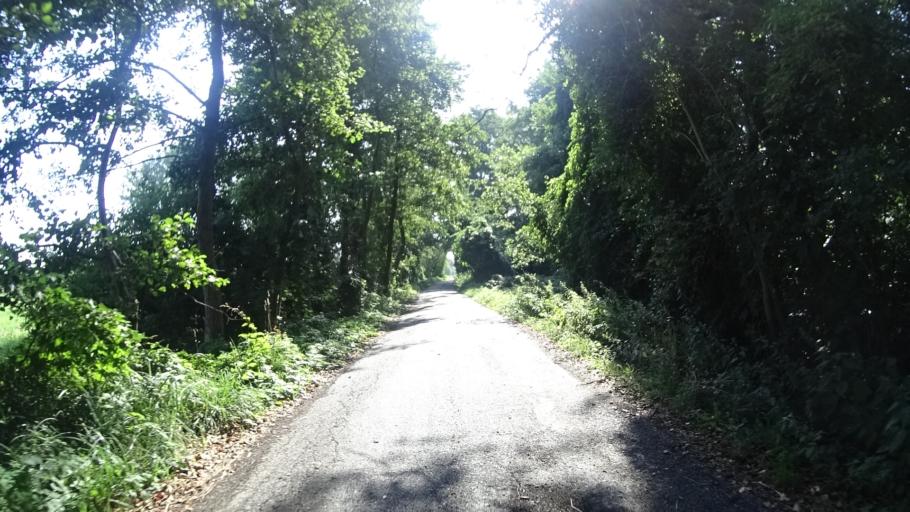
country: DE
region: Brandenburg
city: Neu Zauche
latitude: 51.9039
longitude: 14.0793
